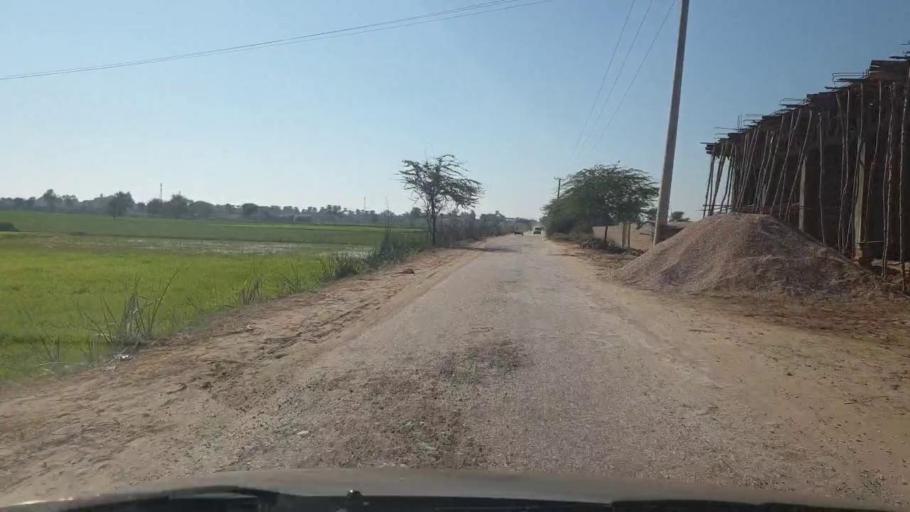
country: PK
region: Sindh
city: Bozdar
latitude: 27.0793
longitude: 68.6182
